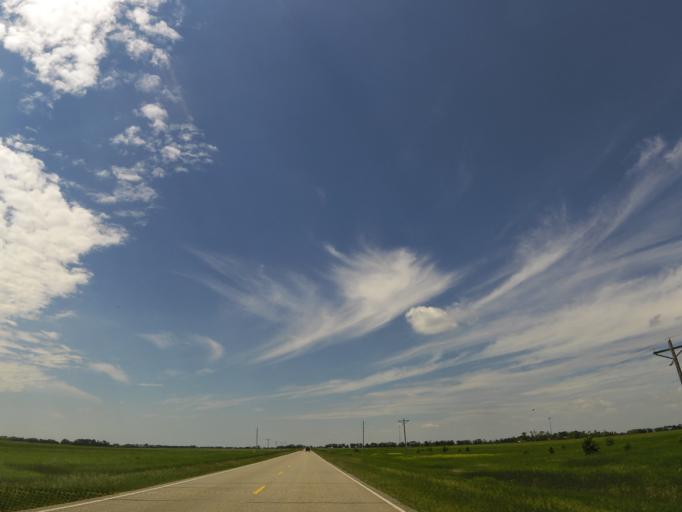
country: US
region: North Dakota
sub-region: Walsh County
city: Grafton
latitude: 48.2953
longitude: -97.2031
